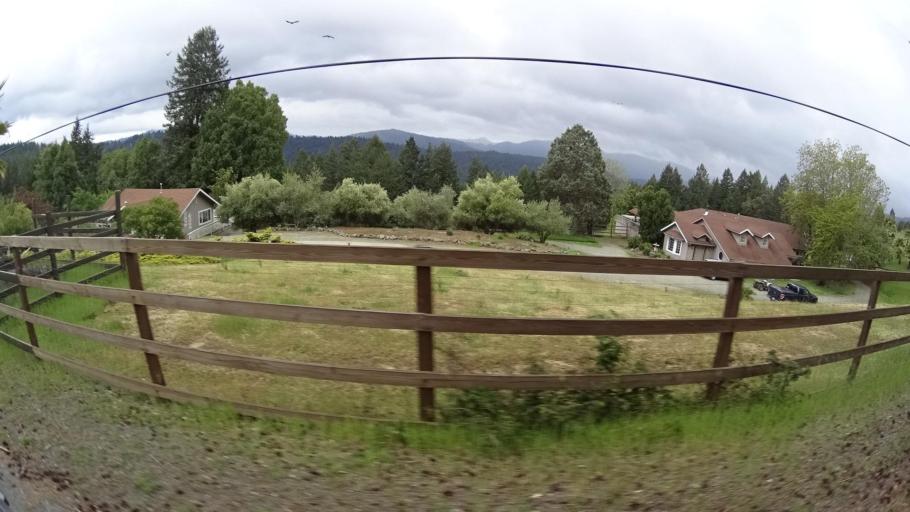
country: US
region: California
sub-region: Humboldt County
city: Redway
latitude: 40.2861
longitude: -123.8004
